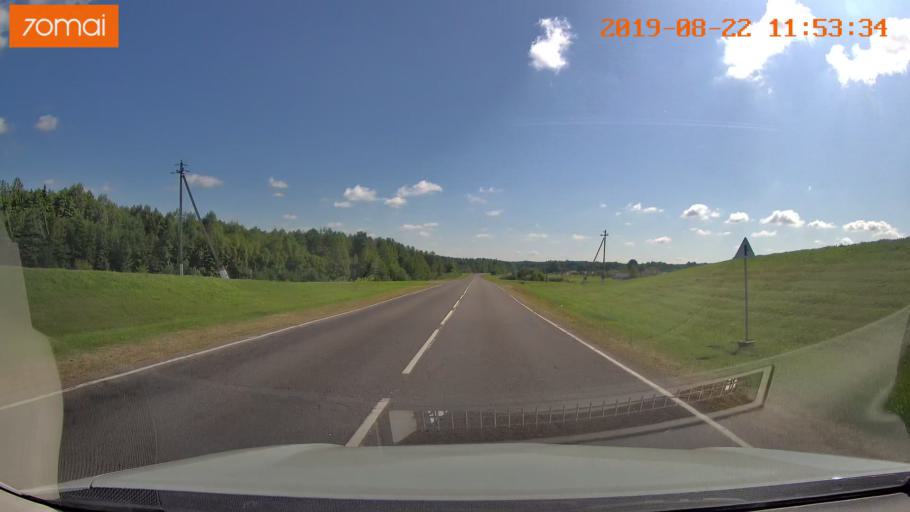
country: BY
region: Minsk
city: Uzda
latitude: 53.4371
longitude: 27.5056
